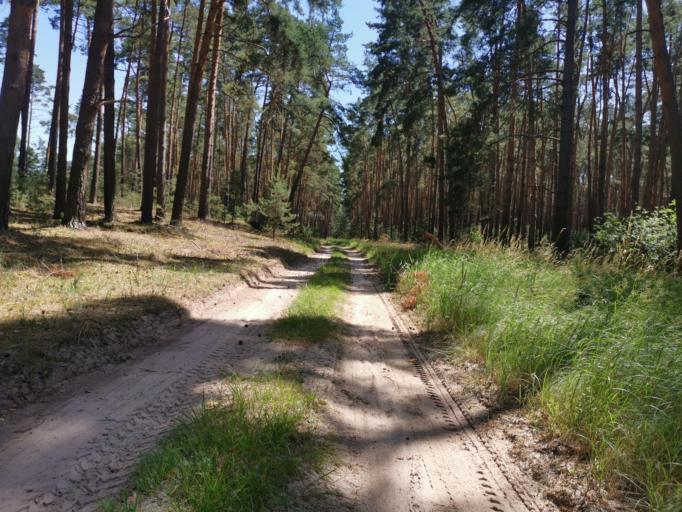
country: CZ
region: South Moravian
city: Vracov
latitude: 48.9552
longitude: 17.2264
